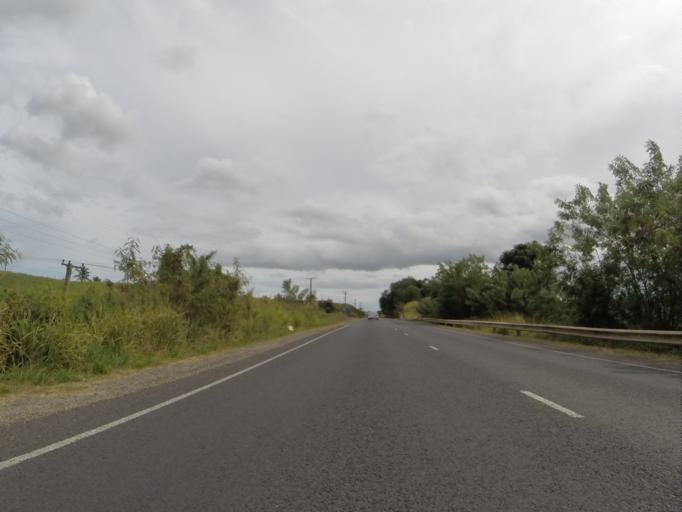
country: FJ
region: Western
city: Nadi
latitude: -18.0508
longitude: 177.3479
